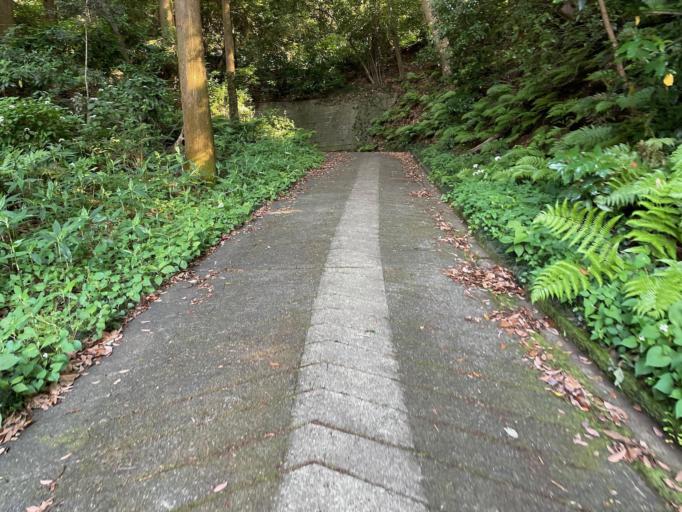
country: JP
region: Saitama
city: Sakado
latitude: 36.0014
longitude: 139.3633
